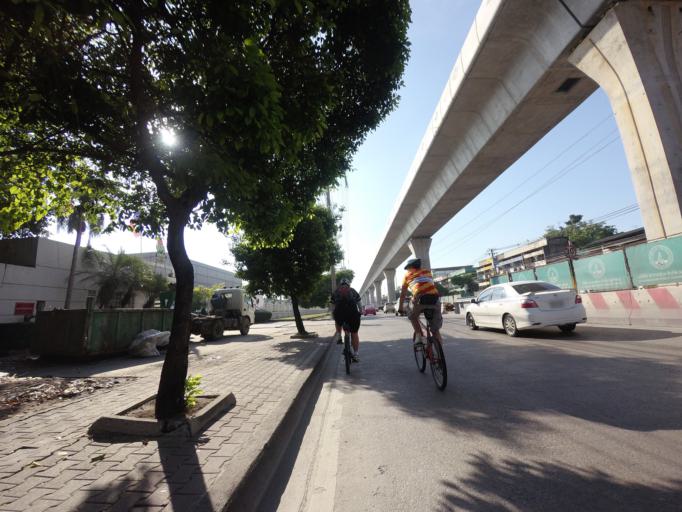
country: TH
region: Samut Prakan
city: Samut Prakan
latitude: 13.6189
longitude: 100.5912
